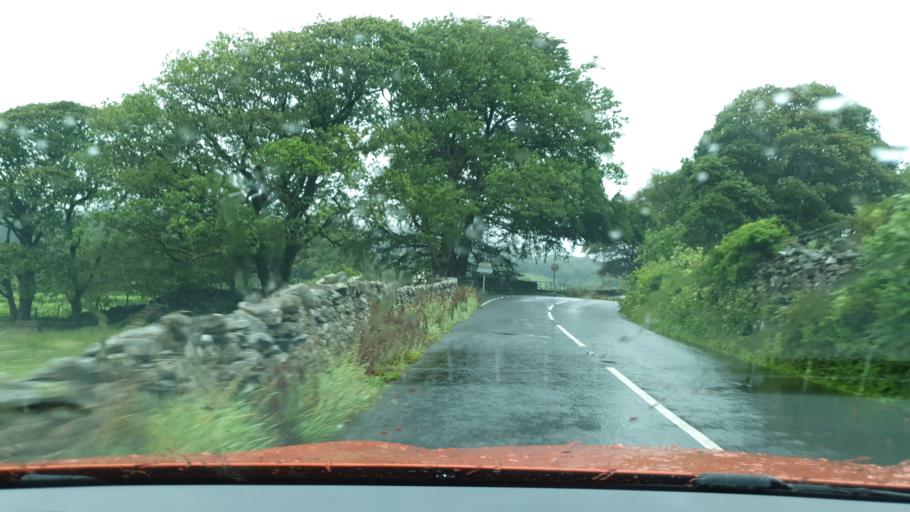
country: GB
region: England
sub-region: Cumbria
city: Ulverston
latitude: 54.3354
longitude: -3.0986
